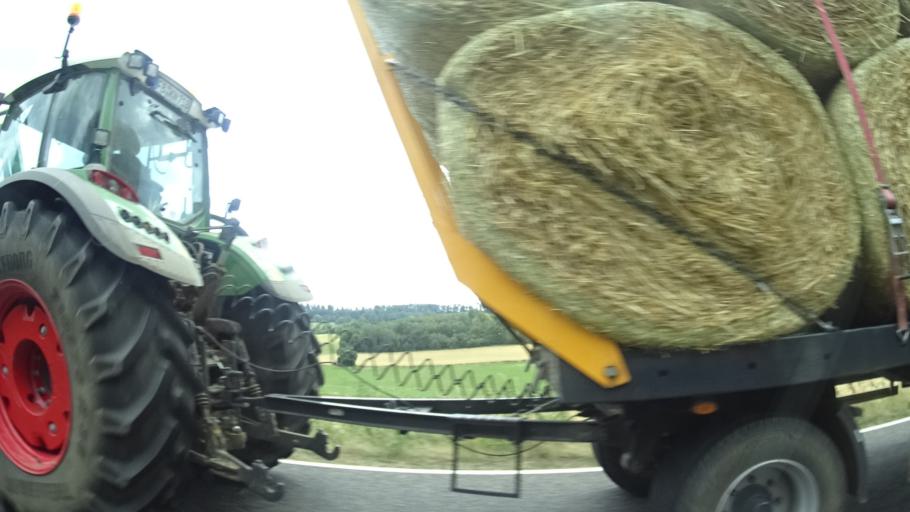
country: DE
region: Hesse
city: Gedern
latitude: 50.4130
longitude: 9.2065
